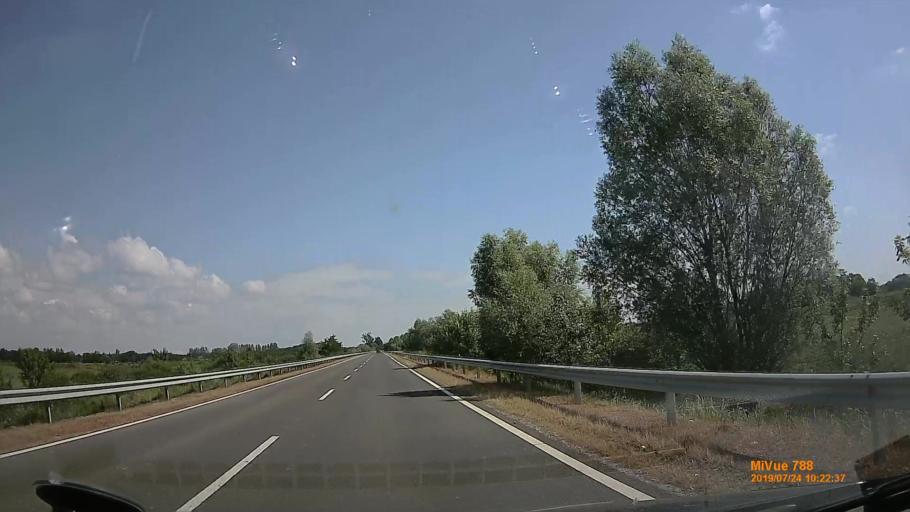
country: HU
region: Szabolcs-Szatmar-Bereg
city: Vasarosnameny
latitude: 48.1387
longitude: 22.3575
